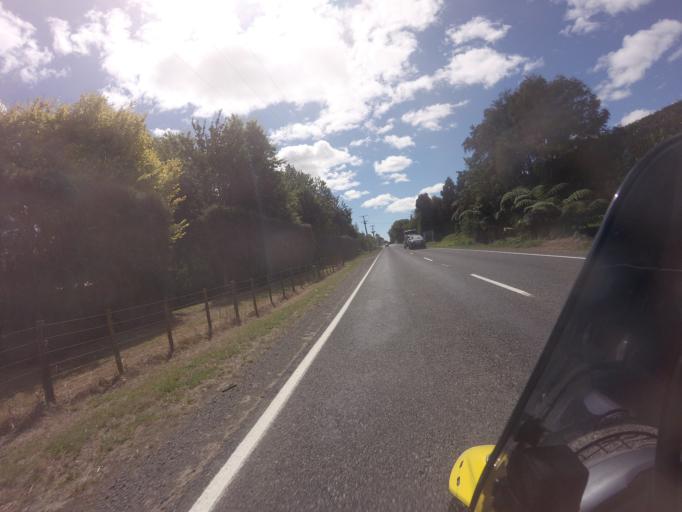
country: NZ
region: Bay of Plenty
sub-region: Whakatane District
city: Edgecumbe
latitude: -38.0257
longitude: 176.8373
